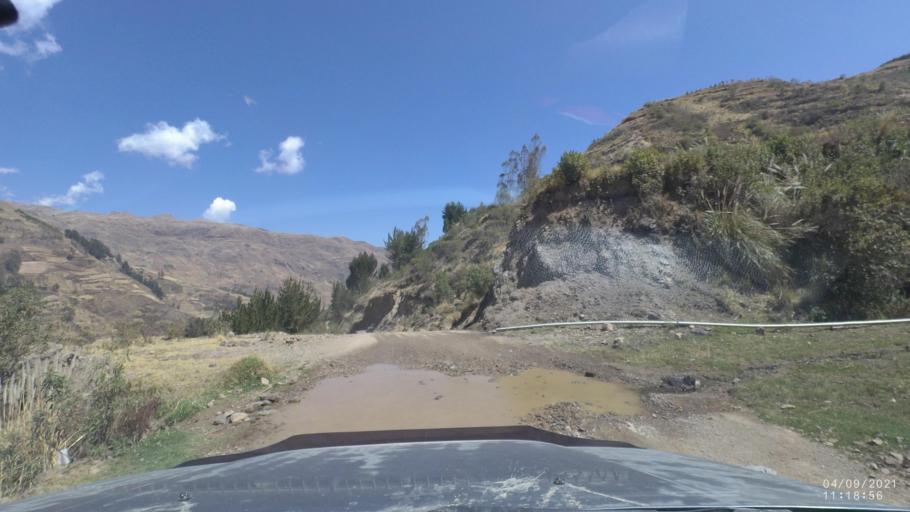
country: BO
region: Cochabamba
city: Sipe Sipe
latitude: -17.2660
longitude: -66.4945
